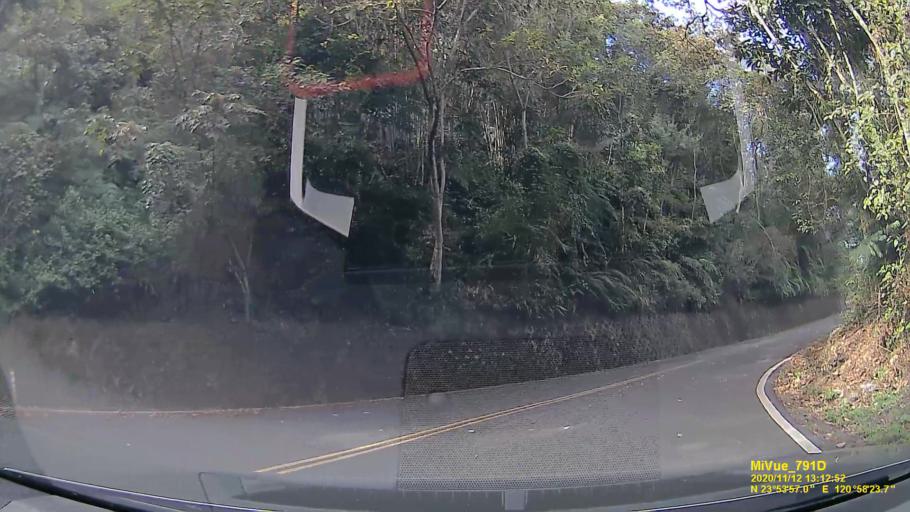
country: TW
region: Taiwan
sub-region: Nantou
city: Puli
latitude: 23.8992
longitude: 120.9732
